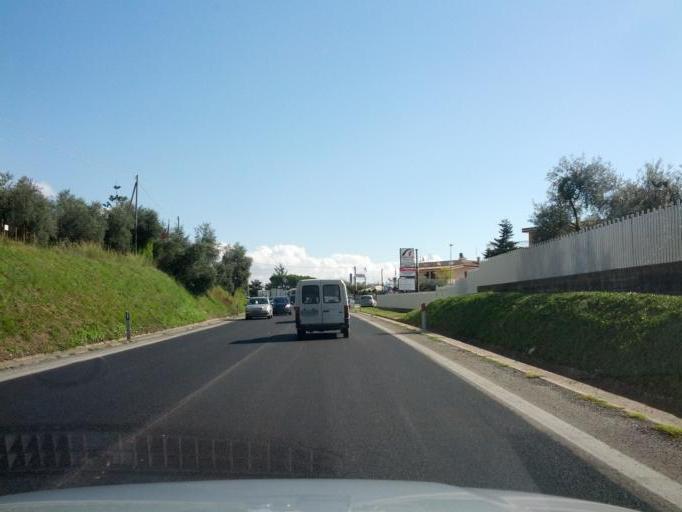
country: IT
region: Latium
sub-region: Provincia di Latina
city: Formia
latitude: 41.2660
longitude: 13.6496
